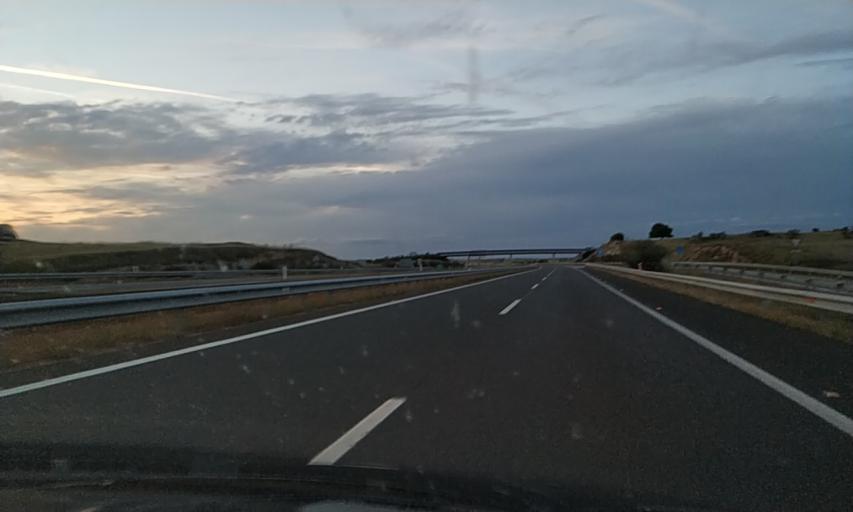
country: ES
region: Extremadura
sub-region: Provincia de Caceres
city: Caceres
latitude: 39.4639
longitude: -6.4222
